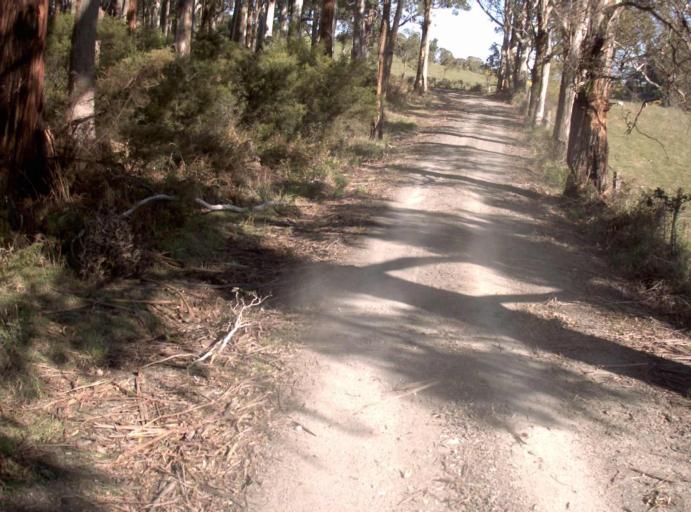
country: AU
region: Tasmania
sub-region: Launceston
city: Mayfield
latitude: -41.2491
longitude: 147.1834
